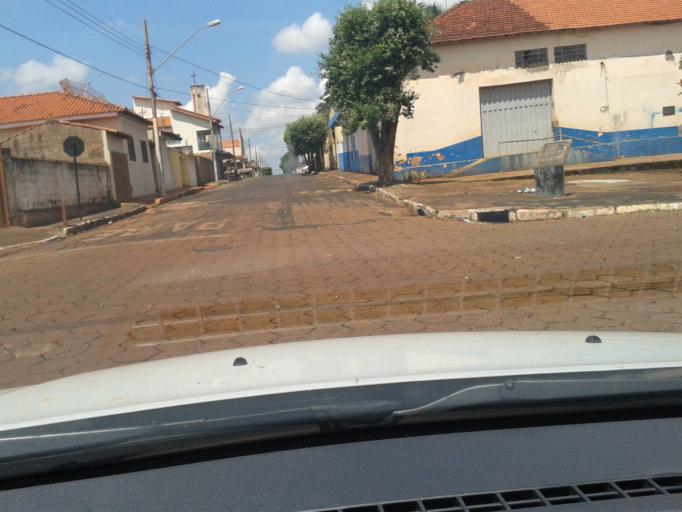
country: BR
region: Minas Gerais
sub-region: Centralina
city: Centralina
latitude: -18.5843
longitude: -49.1972
